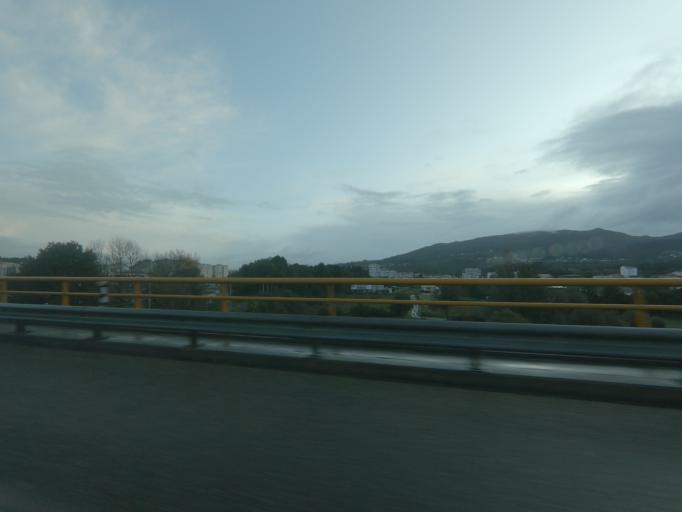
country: PT
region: Viana do Castelo
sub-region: Valenca
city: Valenca
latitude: 42.0193
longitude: -8.6471
